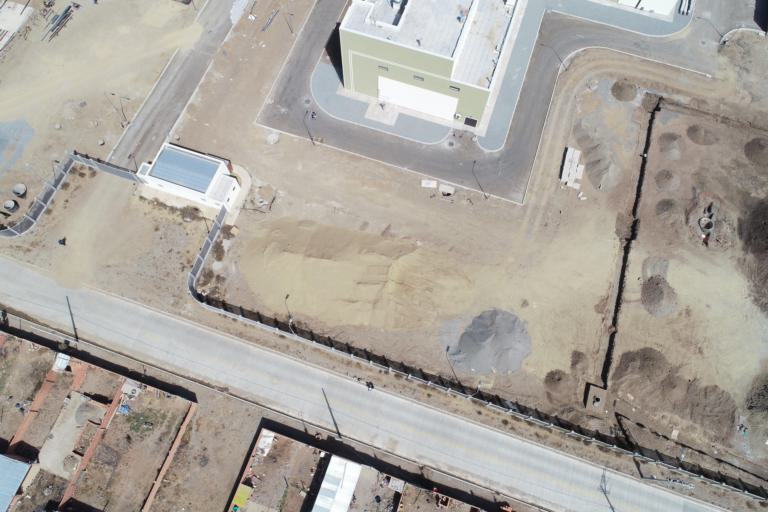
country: BO
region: La Paz
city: La Paz
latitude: -16.5948
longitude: -68.2136
